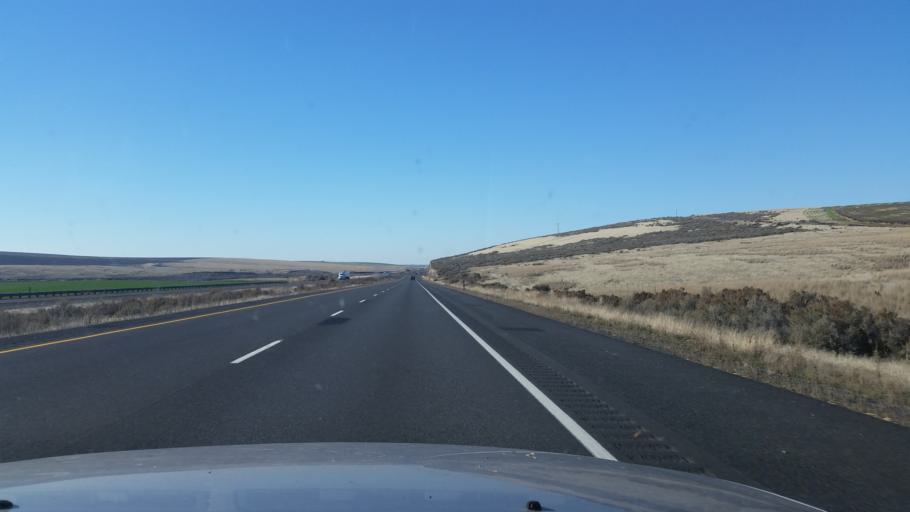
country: US
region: Washington
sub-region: Grant County
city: Warden
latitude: 47.0847
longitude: -118.9715
